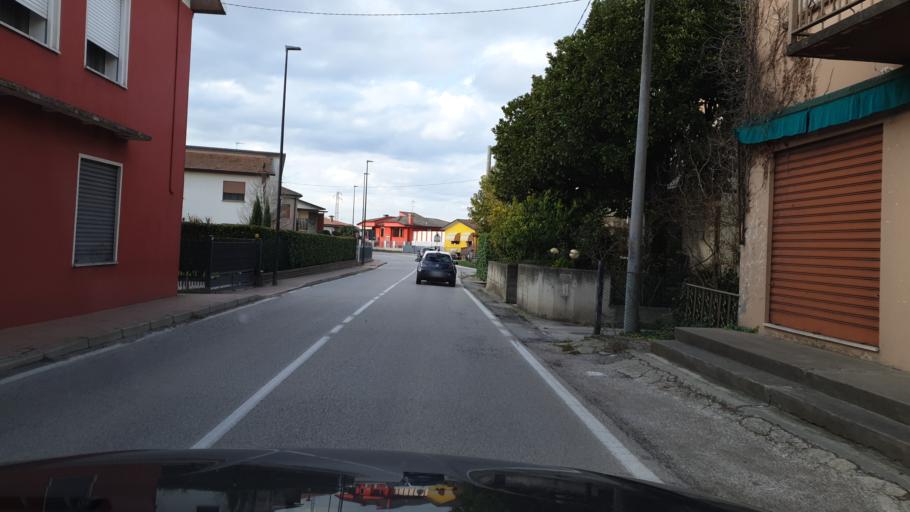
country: IT
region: Veneto
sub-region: Provincia di Rovigo
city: Villanova del Ghebbo Canton
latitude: 45.0576
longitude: 11.6426
